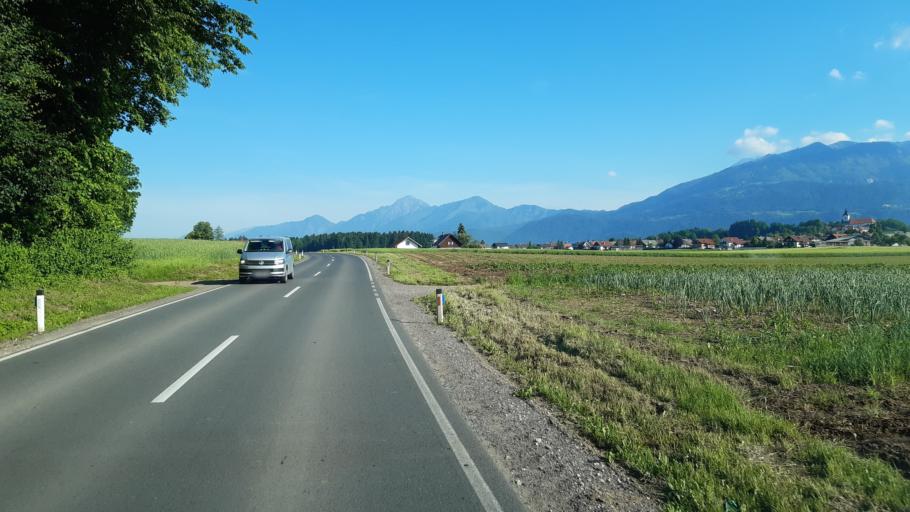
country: SI
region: Komenda
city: Komenda
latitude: 46.1984
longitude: 14.5389
